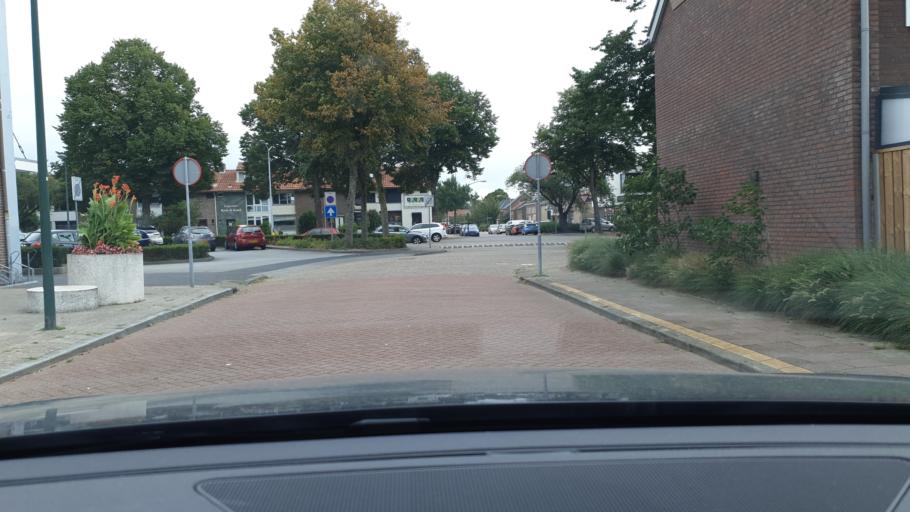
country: NL
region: North Brabant
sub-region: Gemeente Veldhoven
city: Veldhoven
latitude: 51.4124
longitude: 5.4078
